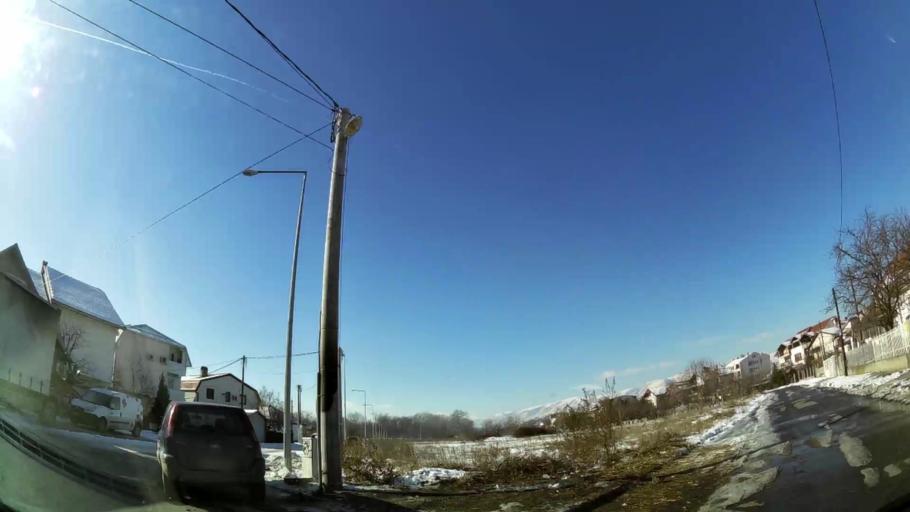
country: MK
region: Saraj
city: Saraj
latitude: 42.0034
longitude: 21.3513
